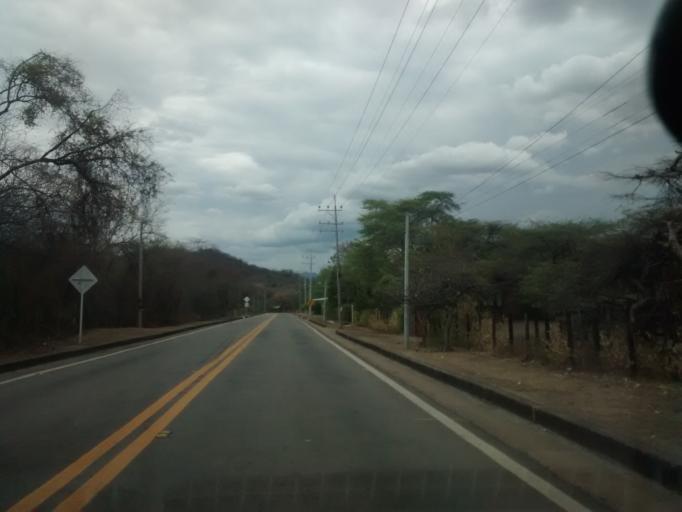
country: CO
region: Cundinamarca
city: Agua de Dios
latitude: 4.4291
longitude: -74.6912
